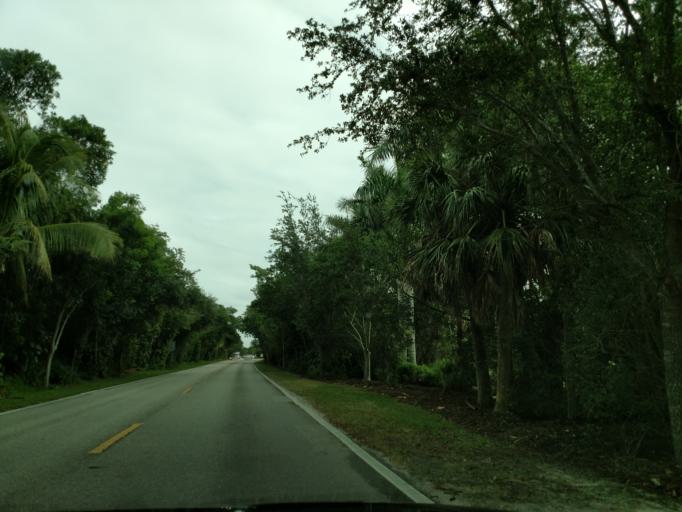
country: US
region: Florida
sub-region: Lee County
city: Sanibel
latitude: 26.4438
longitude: -82.0503
